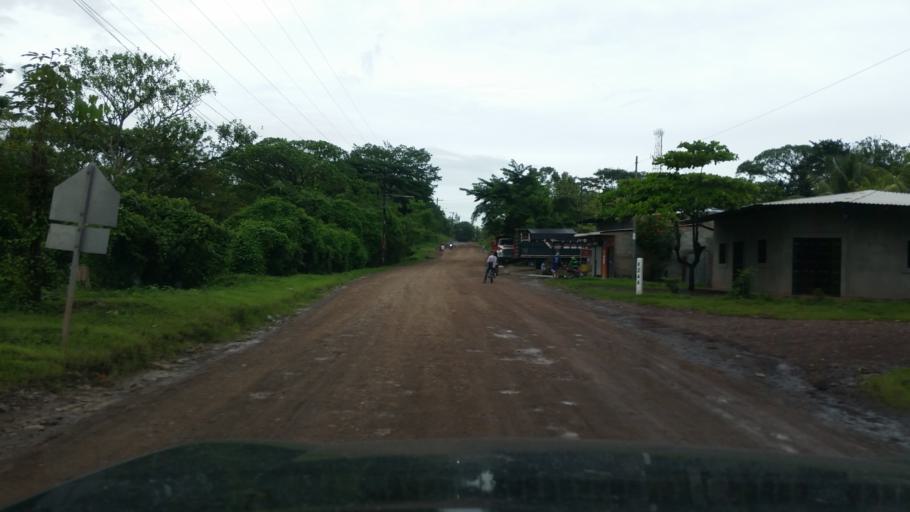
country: NI
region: Matagalpa
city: Rio Blanco
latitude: 13.1668
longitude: -84.9653
